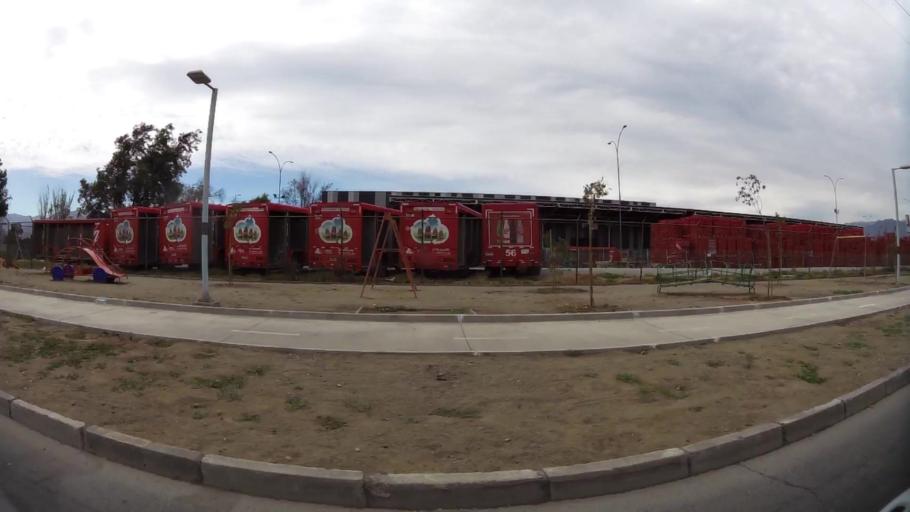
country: CL
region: O'Higgins
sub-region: Provincia de Cachapoal
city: Rancagua
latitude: -34.1459
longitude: -70.7316
